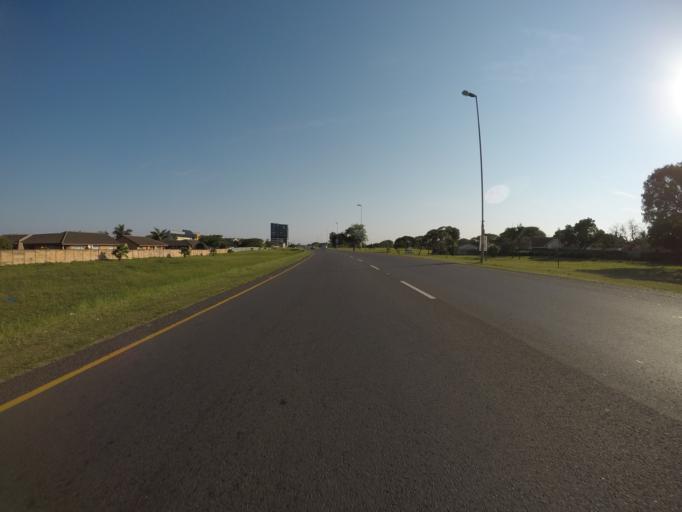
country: ZA
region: KwaZulu-Natal
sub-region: uThungulu District Municipality
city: Richards Bay
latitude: -28.7533
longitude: 32.0573
